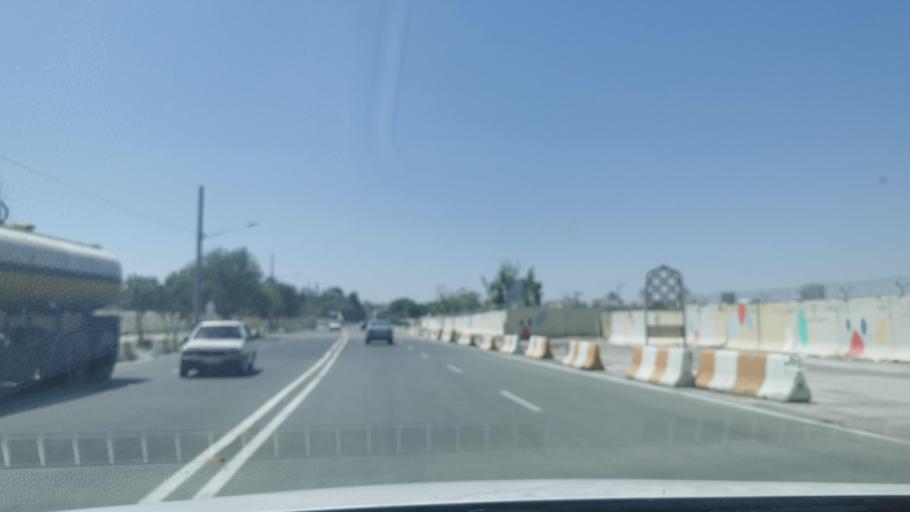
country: IR
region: Razavi Khorasan
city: Mashhad
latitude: 36.2735
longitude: 59.5833
